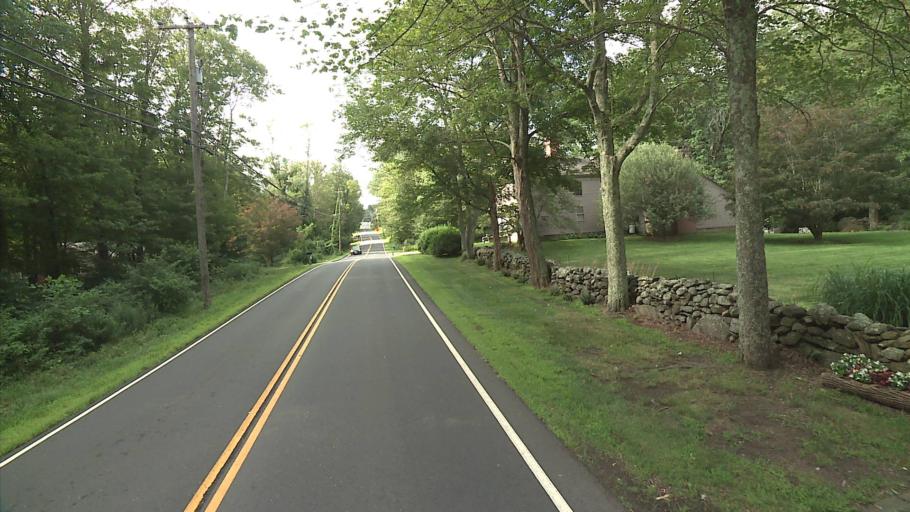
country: US
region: Connecticut
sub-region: Middlesex County
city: Moodus
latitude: 41.5505
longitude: -72.4126
